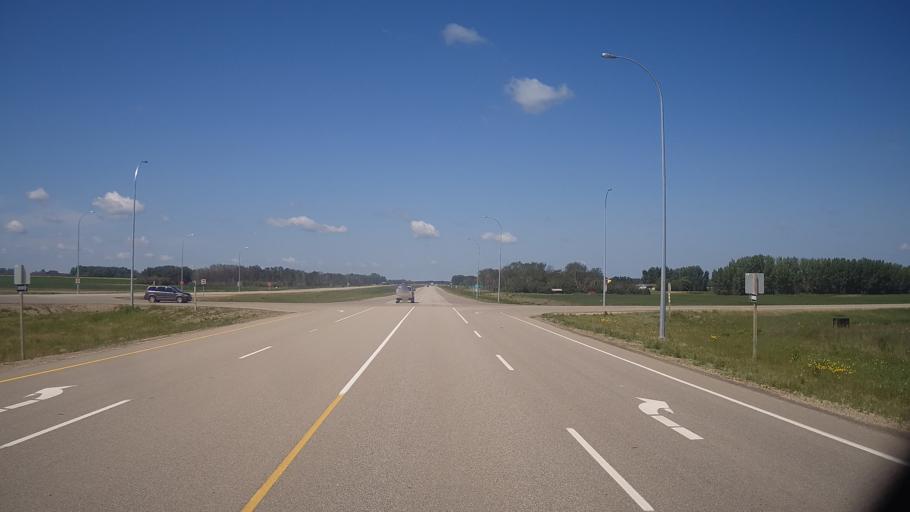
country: CA
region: Saskatchewan
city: Saskatoon
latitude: 52.0123
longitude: -106.3839
